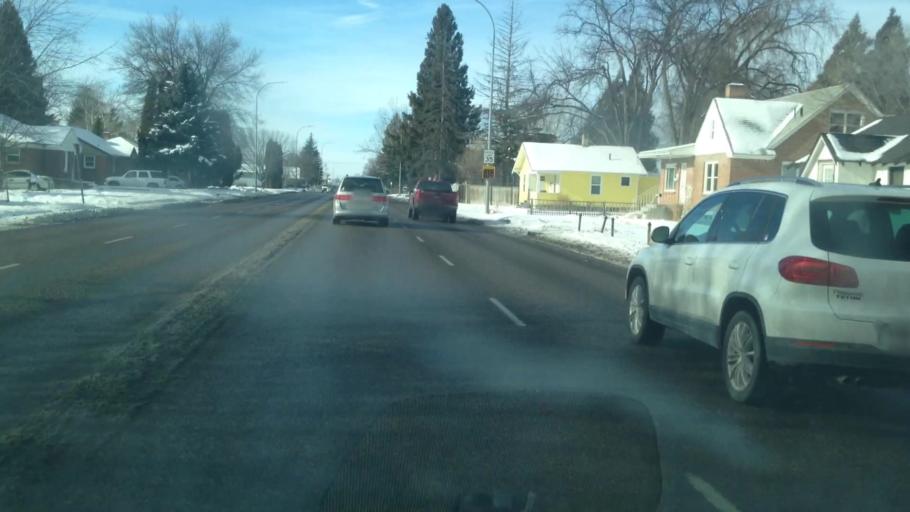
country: US
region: Idaho
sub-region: Bonneville County
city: Idaho Falls
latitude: 43.4826
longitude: -112.0365
